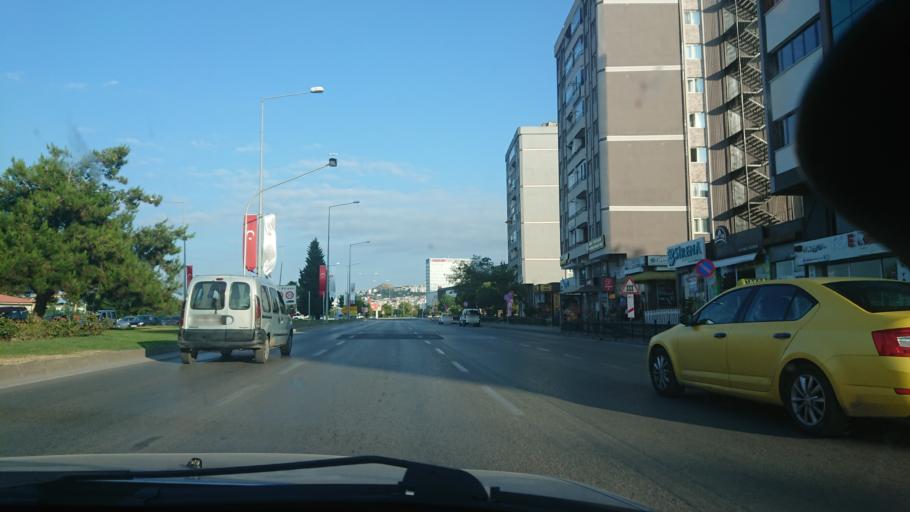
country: TR
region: Samsun
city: Samsun
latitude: 41.2803
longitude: 36.3491
